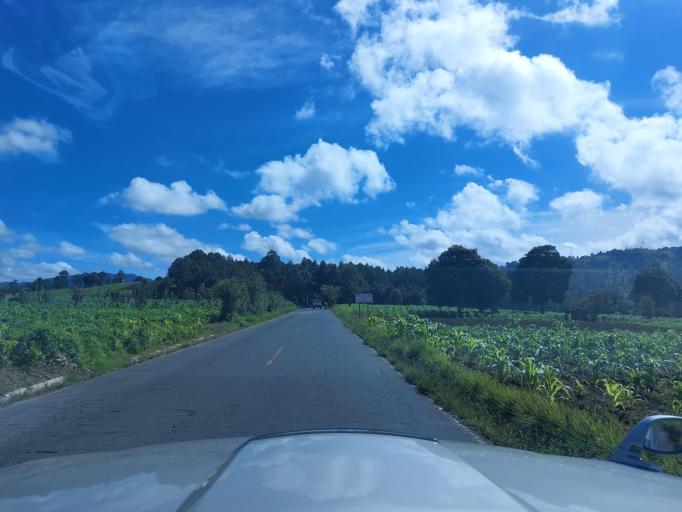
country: GT
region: Chimaltenango
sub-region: Municipio de Santa Cruz Balanya
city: Santa Cruz Balanya
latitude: 14.7037
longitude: -90.8977
